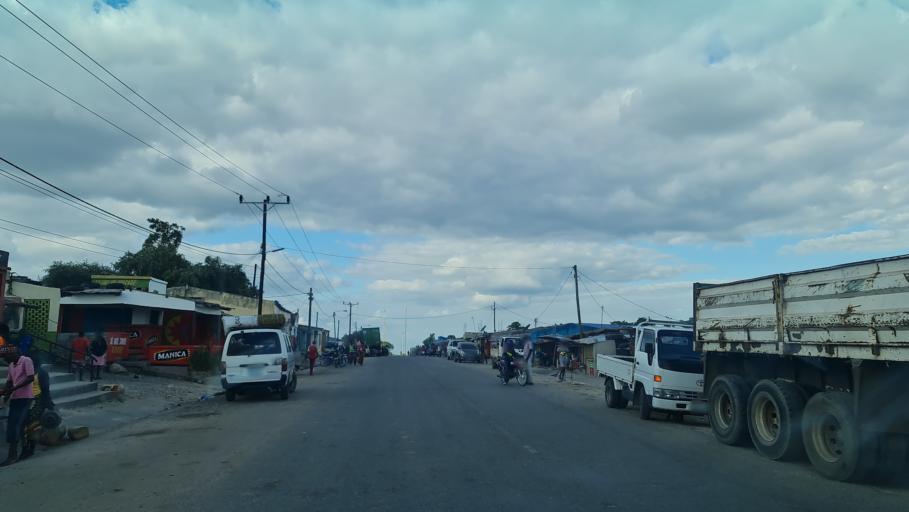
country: MZ
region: Manica
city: Chimoio
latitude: -19.2098
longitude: 33.9277
